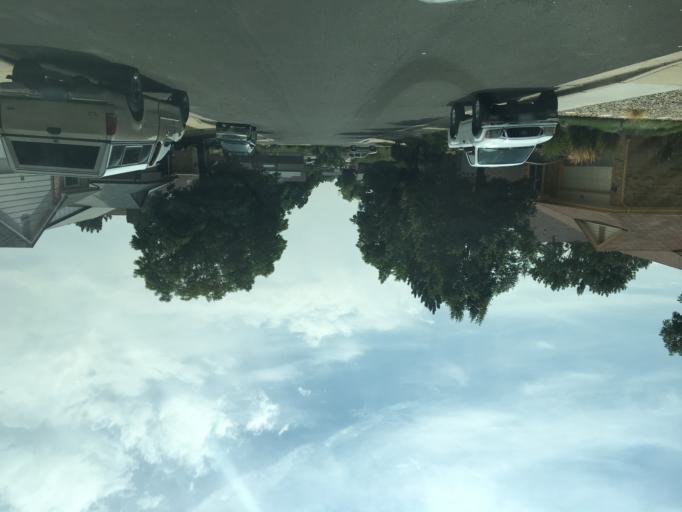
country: US
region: Colorado
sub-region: Adams County
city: Aurora
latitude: 39.7290
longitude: -104.8018
